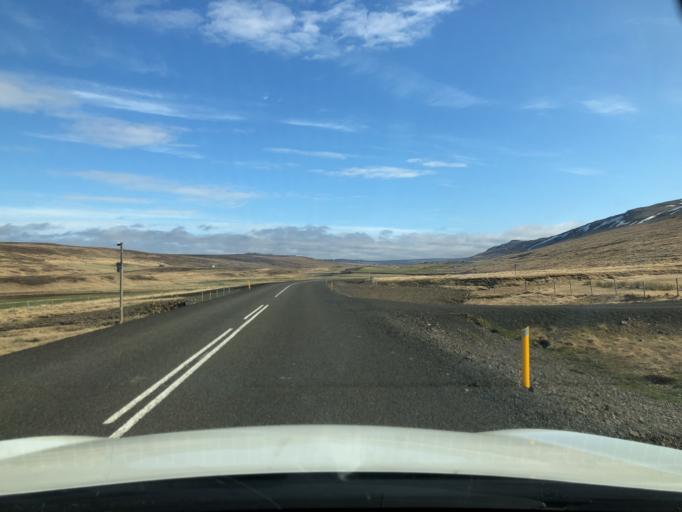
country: IS
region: West
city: Borgarnes
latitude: 65.1354
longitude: -21.6073
